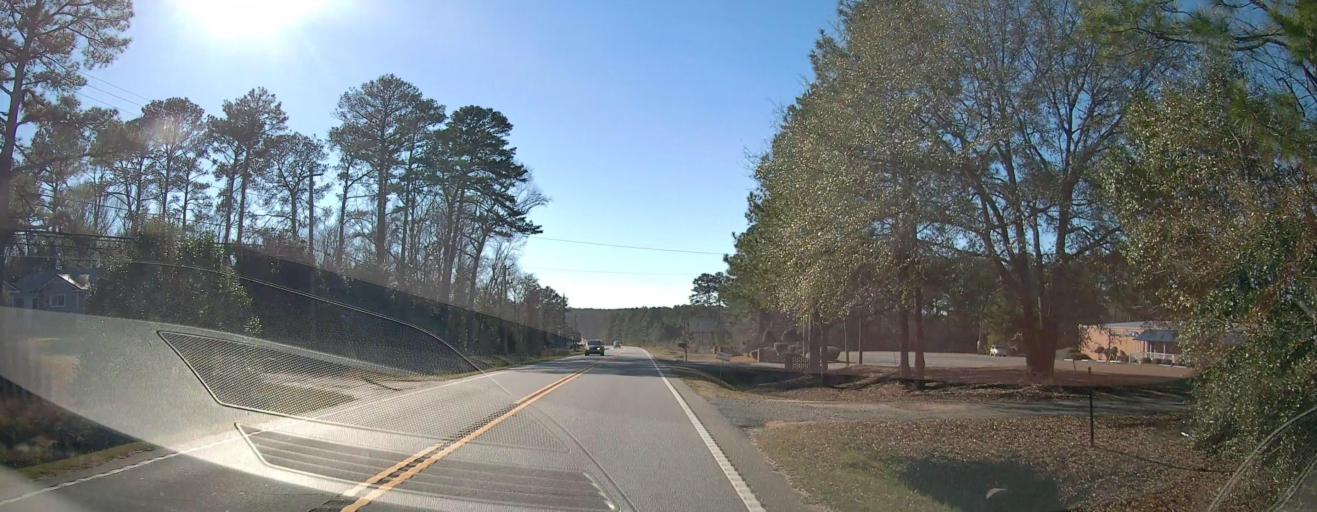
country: US
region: Georgia
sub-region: Sumter County
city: Americus
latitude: 32.0847
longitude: -84.2491
